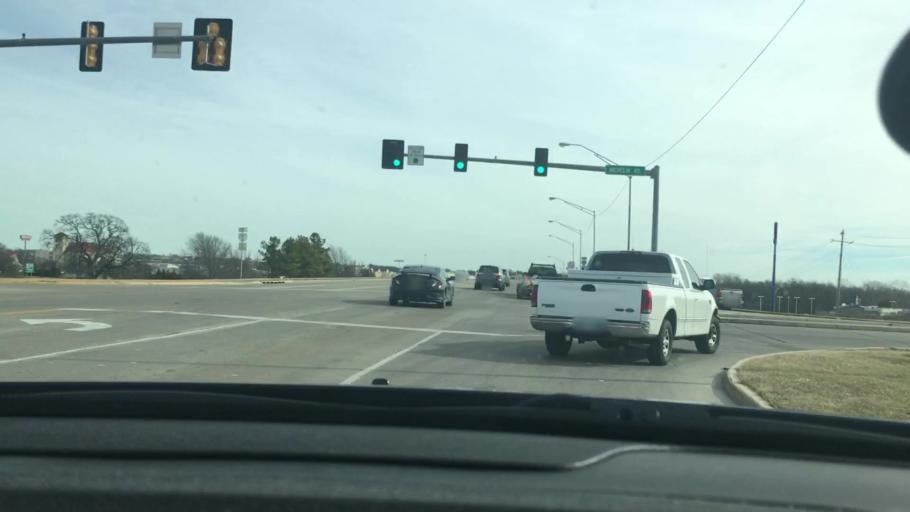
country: US
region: Oklahoma
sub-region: Carter County
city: Ardmore
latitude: 34.1874
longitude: -97.1691
